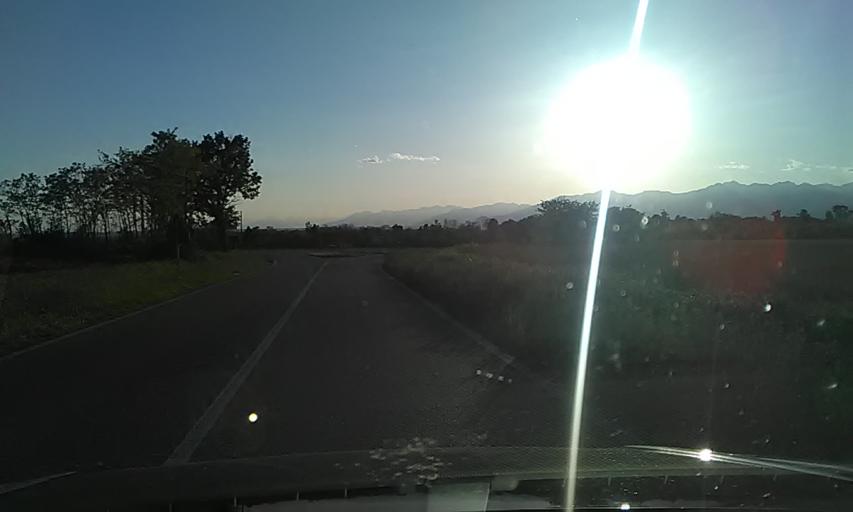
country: IT
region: Piedmont
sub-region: Provincia di Vercelli
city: Rovasenda
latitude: 45.5265
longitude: 8.3200
